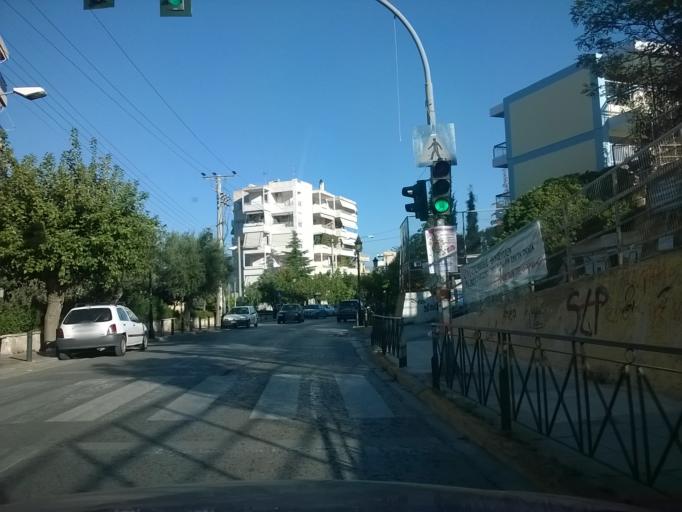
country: GR
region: Attica
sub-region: Nomarchia Athinas
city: Cholargos
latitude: 37.9985
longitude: 23.8064
